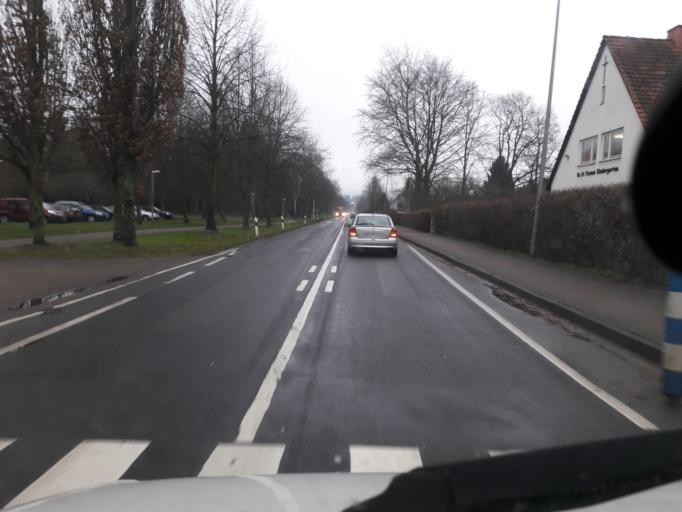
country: DE
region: North Rhine-Westphalia
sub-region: Regierungsbezirk Detmold
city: Minden
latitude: 52.2789
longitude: 8.8878
